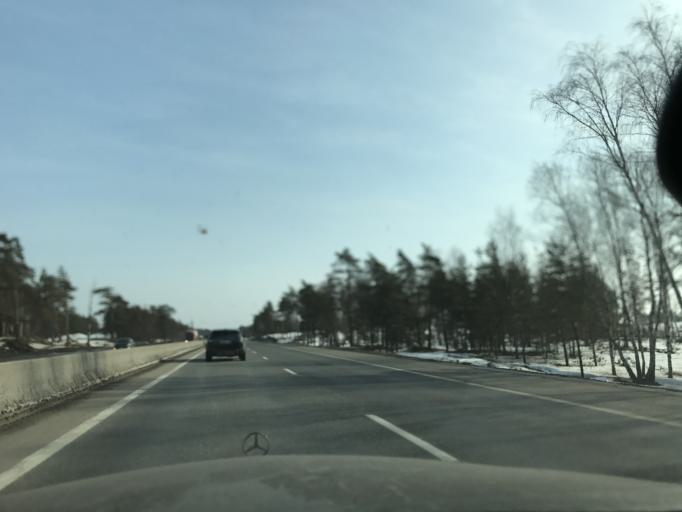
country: RU
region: Nizjnij Novgorod
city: Babino
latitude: 56.3012
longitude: 43.5484
